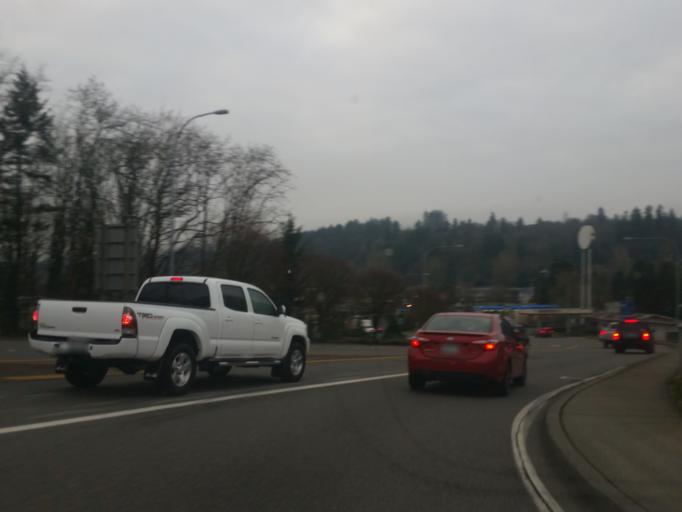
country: US
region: Washington
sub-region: King County
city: Woodinville
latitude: 47.7573
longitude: -122.1647
